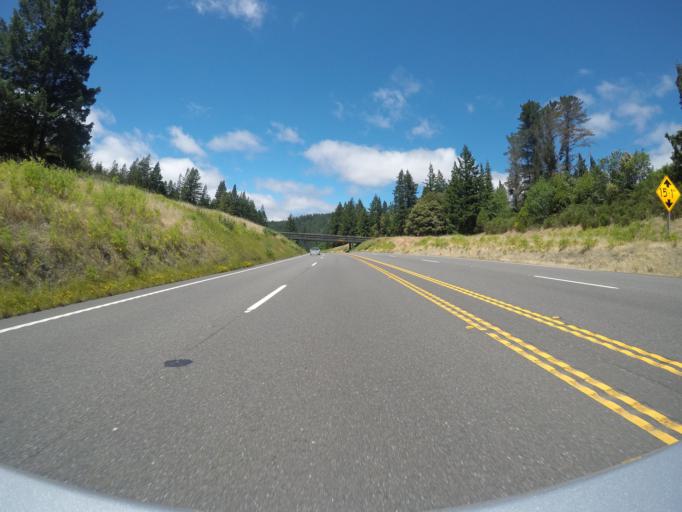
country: US
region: California
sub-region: Humboldt County
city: Redway
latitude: 40.2498
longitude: -123.8317
